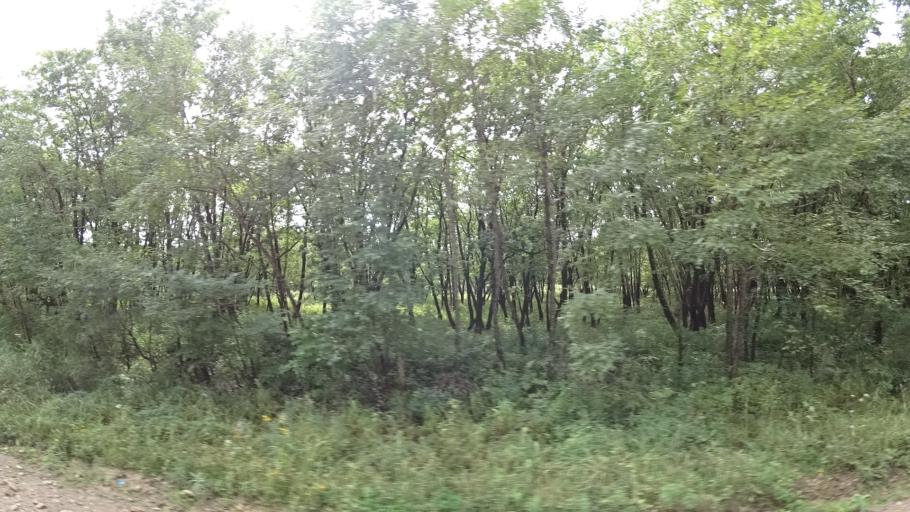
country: RU
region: Primorskiy
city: Lyalichi
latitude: 44.0933
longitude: 132.4326
